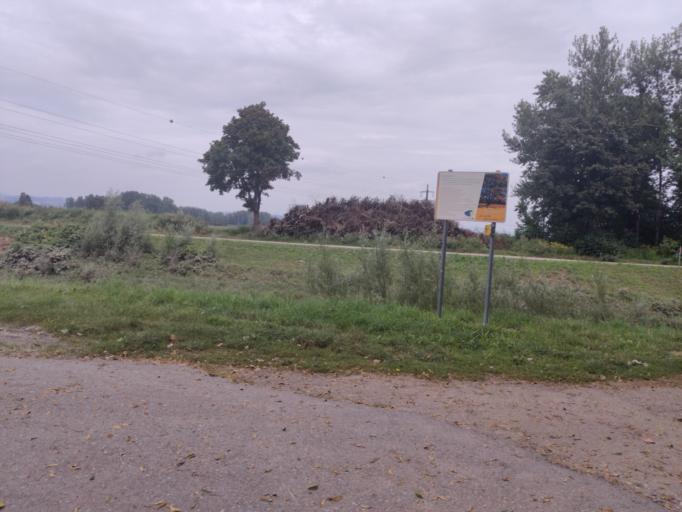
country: AT
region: Lower Austria
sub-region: Politischer Bezirk Amstetten
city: Strengberg
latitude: 48.1824
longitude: 14.7219
